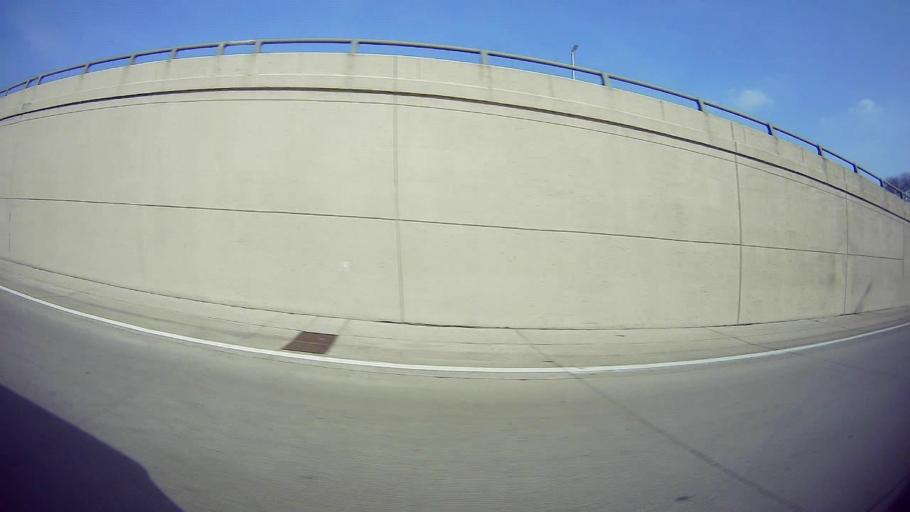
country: US
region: Michigan
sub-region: Oakland County
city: Oak Park
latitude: 42.4478
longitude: -83.2064
